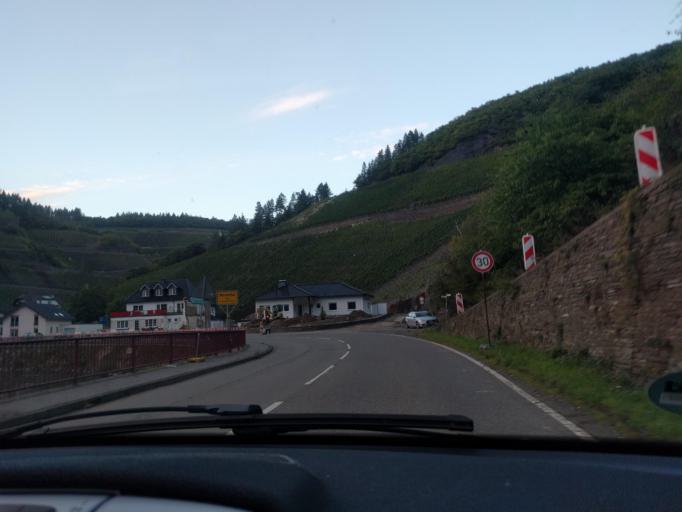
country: DE
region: Rheinland-Pfalz
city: Dernau
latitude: 50.5343
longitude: 7.0597
